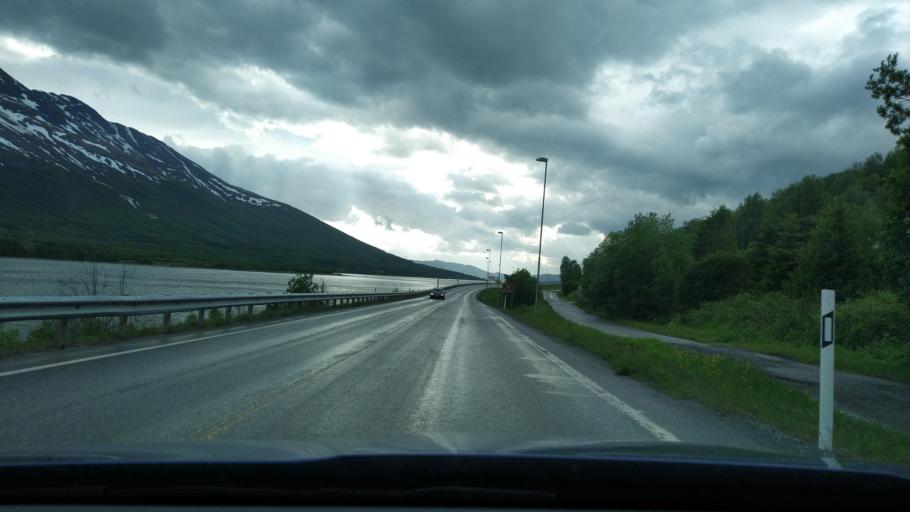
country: NO
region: Troms
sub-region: Balsfjord
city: Storsteinnes
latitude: 69.2219
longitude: 19.5207
